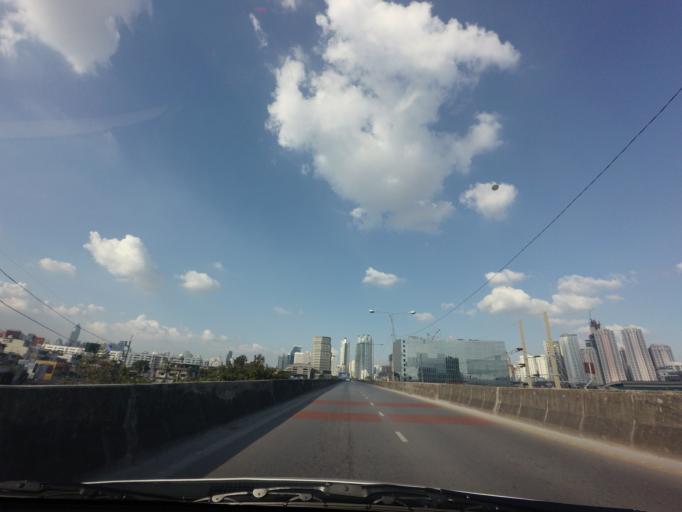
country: TH
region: Bangkok
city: Khlong Toei
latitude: 13.7182
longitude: 100.5583
